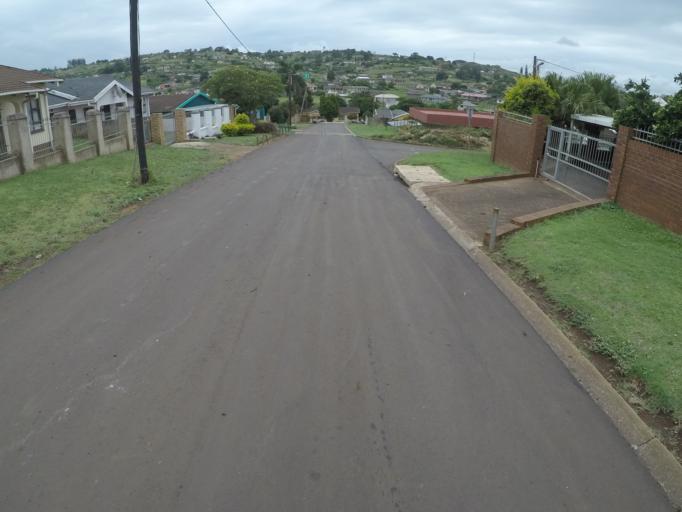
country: ZA
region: KwaZulu-Natal
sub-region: uThungulu District Municipality
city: Empangeni
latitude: -28.7761
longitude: 31.8514
